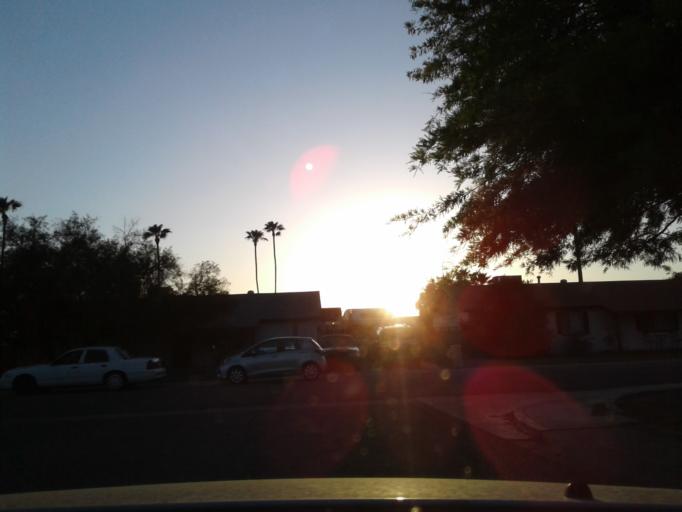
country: US
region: Arizona
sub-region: Maricopa County
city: Glendale
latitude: 33.6097
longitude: -112.0971
